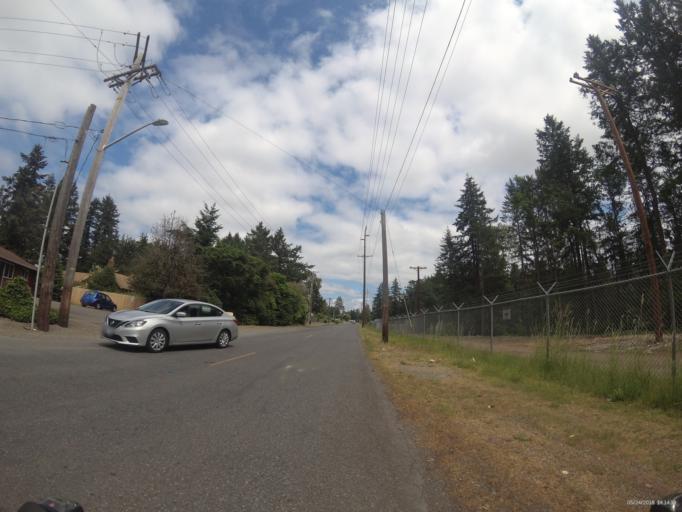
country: US
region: Washington
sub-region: Pierce County
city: McChord Air Force Base
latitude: 47.1394
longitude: -122.5051
